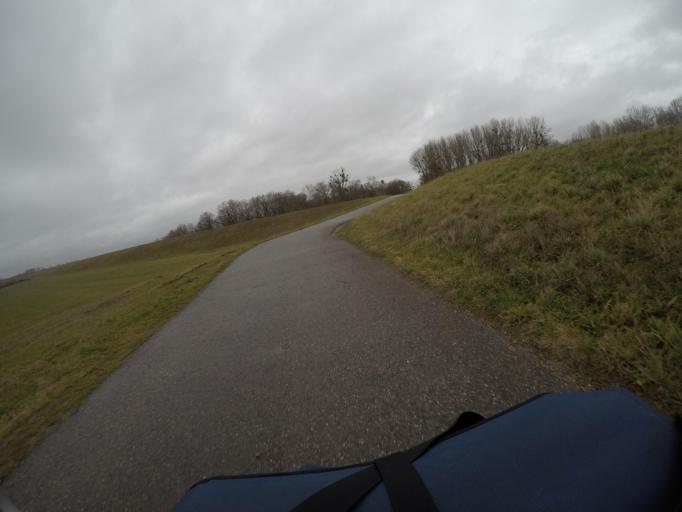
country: DE
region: Rheinland-Pfalz
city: Neupotz
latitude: 49.0932
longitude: 8.3442
